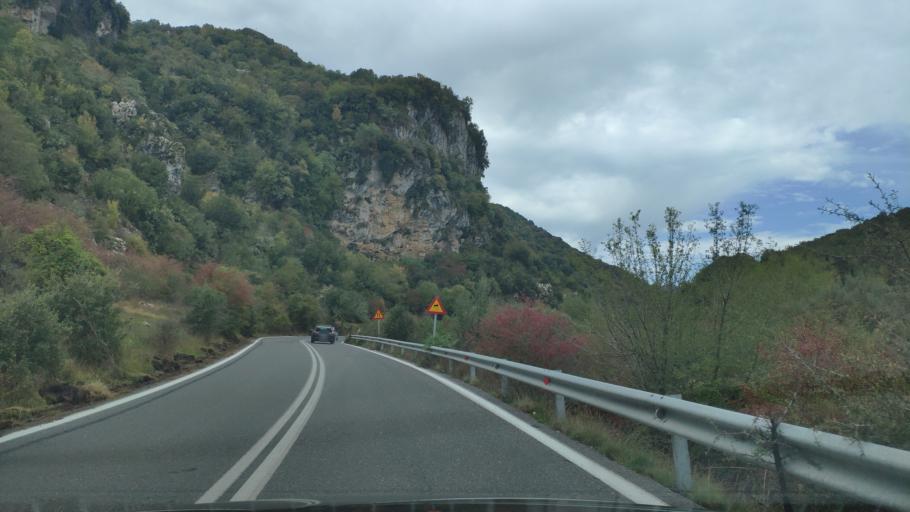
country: GR
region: Peloponnese
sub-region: Nomos Arkadias
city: Dimitsana
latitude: 37.6270
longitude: 22.0621
